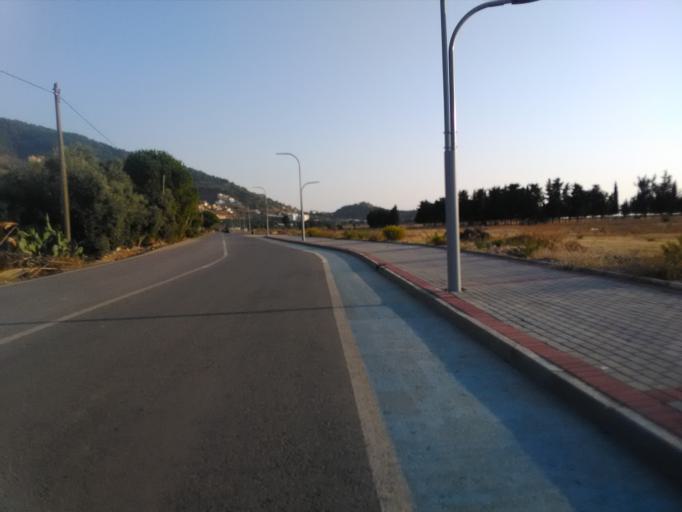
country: TR
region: Antalya
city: Gazipasa
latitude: 36.2471
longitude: 32.2950
